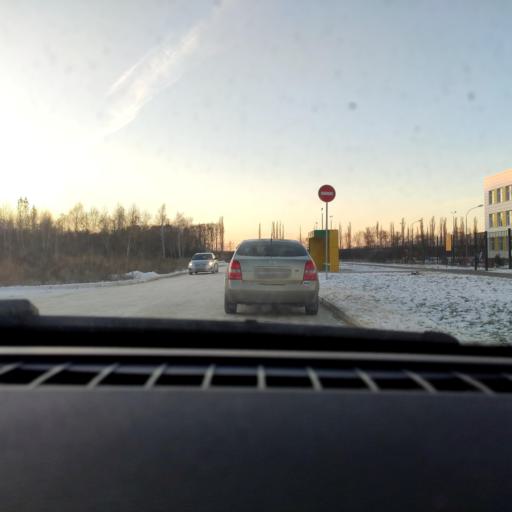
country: RU
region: Voronezj
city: Maslovka
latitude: 51.6324
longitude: 39.2957
